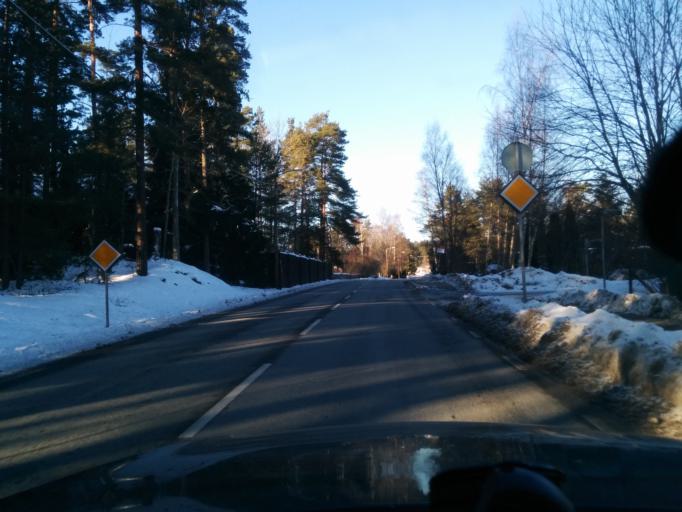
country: SE
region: Stockholm
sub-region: Taby Kommun
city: Taby
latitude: 59.4733
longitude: 18.0971
